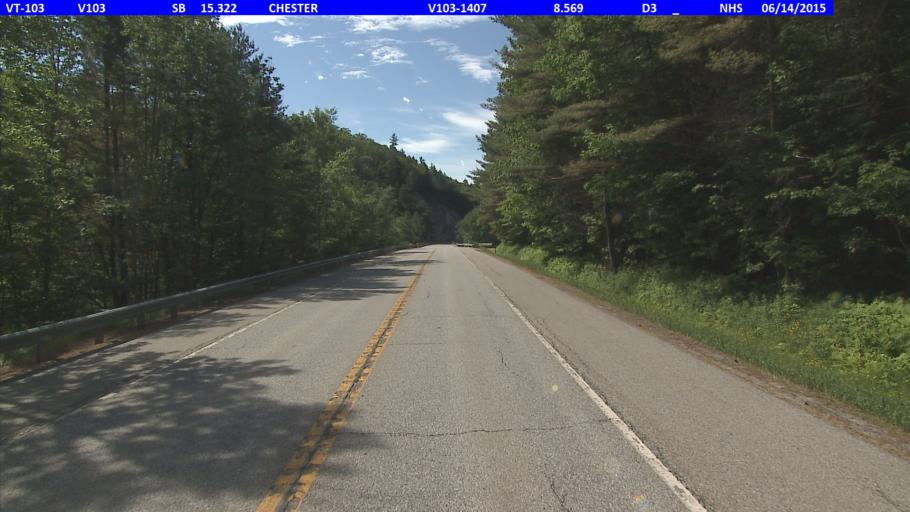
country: US
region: Vermont
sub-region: Windsor County
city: Chester
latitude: 43.3341
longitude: -72.6159
